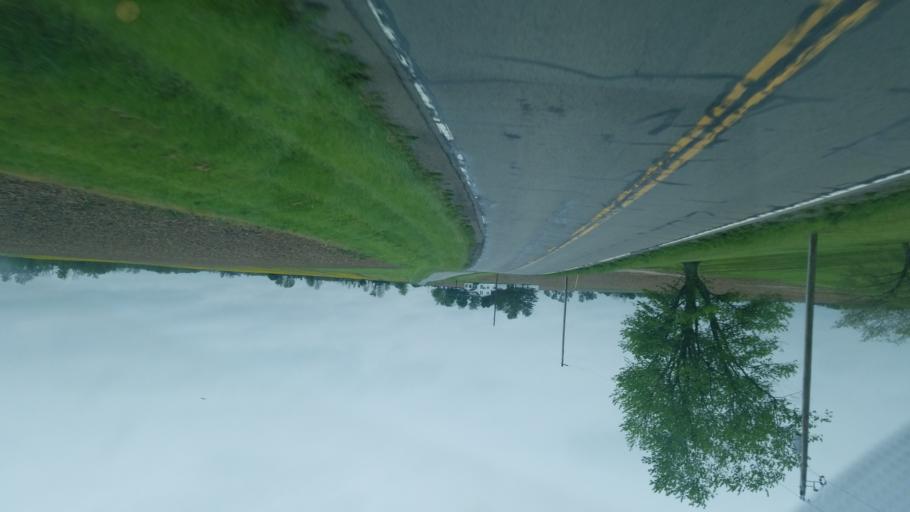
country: US
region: Ohio
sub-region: Highland County
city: Leesburg
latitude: 39.3253
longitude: -83.5557
